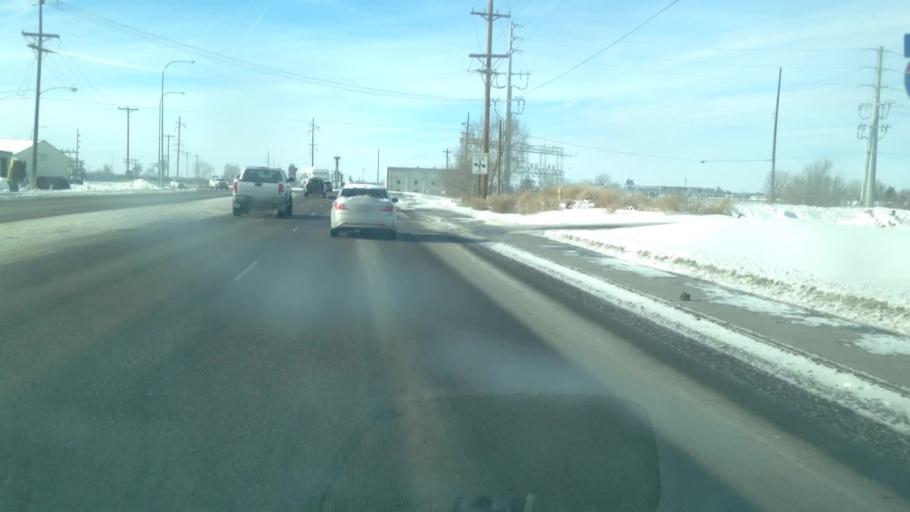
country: US
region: Idaho
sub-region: Bonneville County
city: Idaho Falls
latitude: 43.4684
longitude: -112.0587
